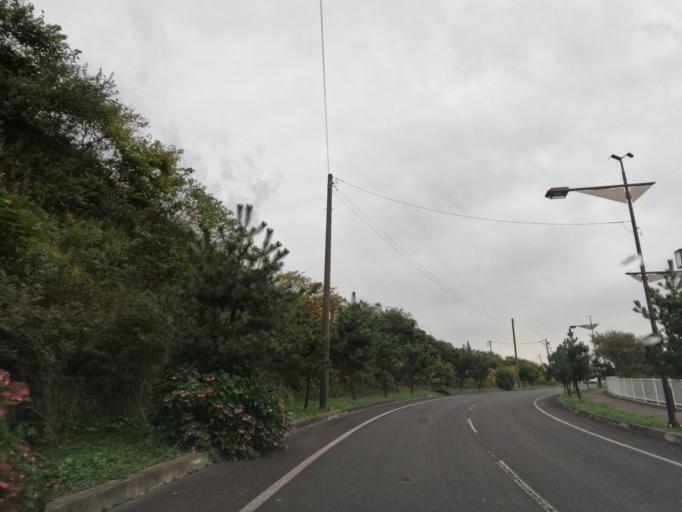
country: JP
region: Hokkaido
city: Muroran
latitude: 42.3373
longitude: 140.9338
